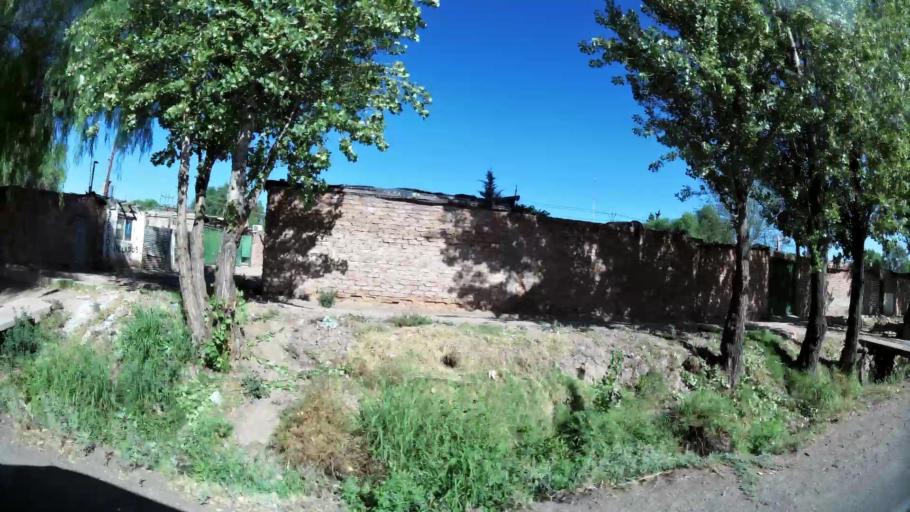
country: AR
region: Mendoza
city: Mendoza
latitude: -32.8788
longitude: -68.8737
